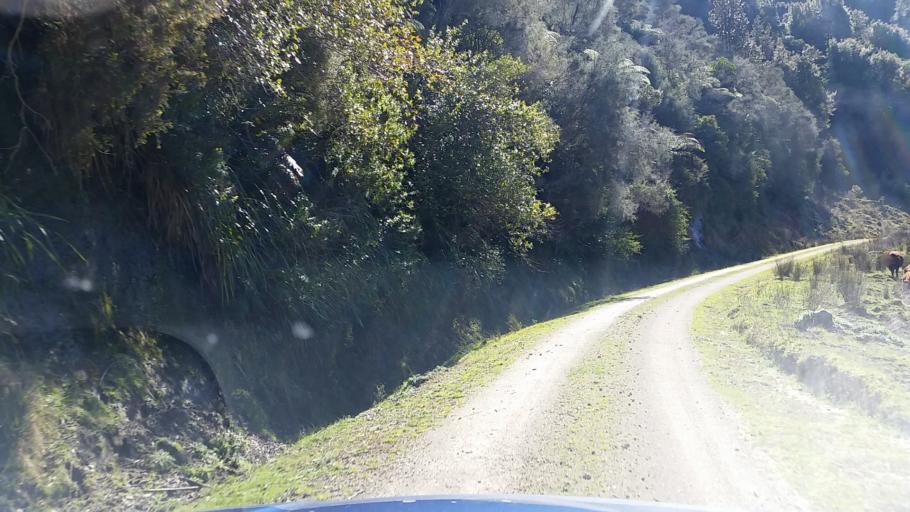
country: NZ
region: Manawatu-Wanganui
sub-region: Wanganui District
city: Wanganui
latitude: -39.6670
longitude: 174.8556
